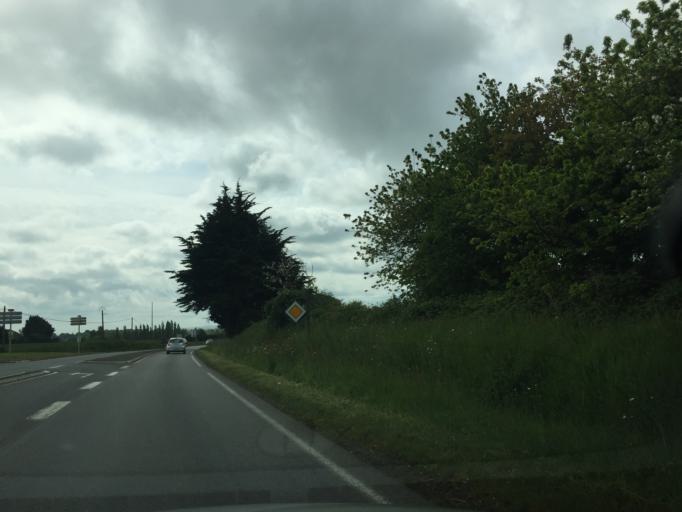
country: FR
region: Brittany
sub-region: Departement des Cotes-d'Armor
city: Saint-Cast-le-Guildo
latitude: 48.5926
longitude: -2.2484
